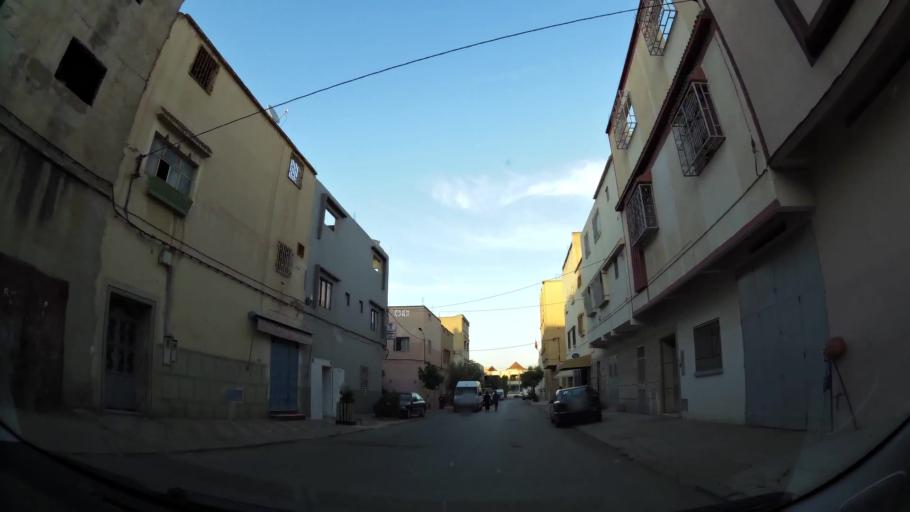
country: MA
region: Oriental
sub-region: Oujda-Angad
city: Oujda
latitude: 34.7000
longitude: -1.9206
